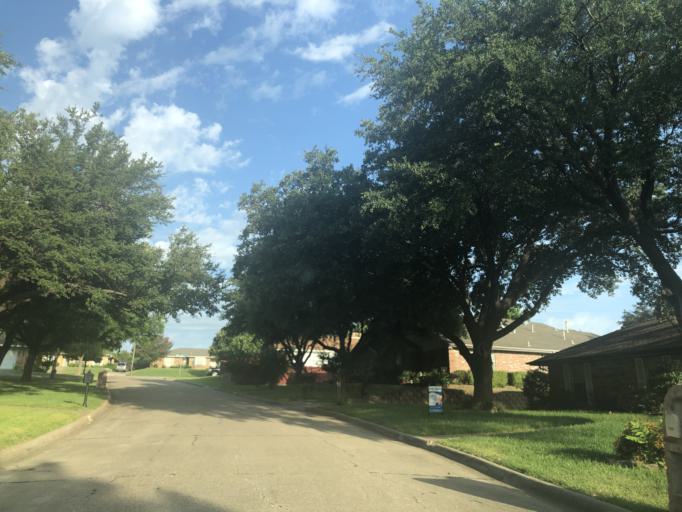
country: US
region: Texas
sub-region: Dallas County
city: Grand Prairie
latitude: 32.7677
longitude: -97.0306
